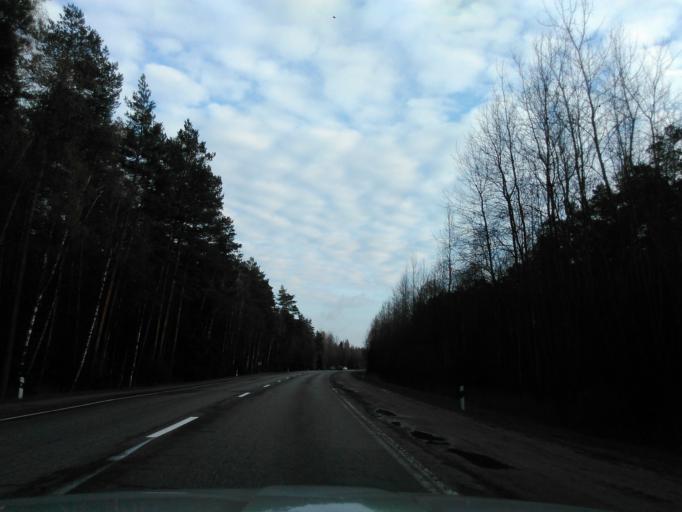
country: BY
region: Minsk
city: Plyeshchanitsy
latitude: 54.3736
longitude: 27.8821
